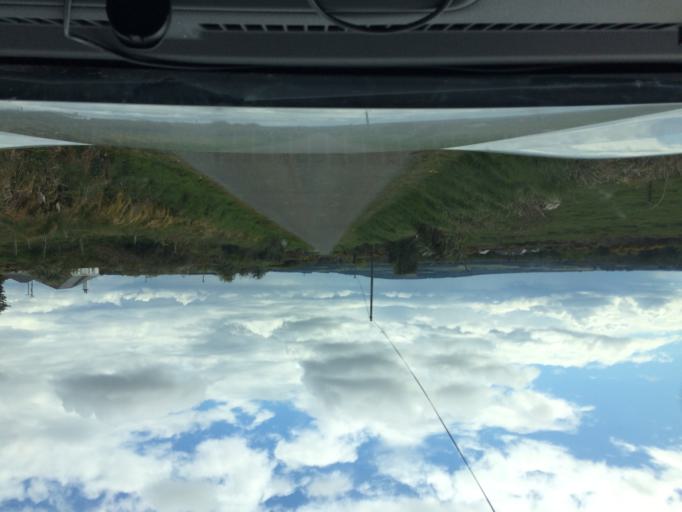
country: IE
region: Munster
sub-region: Waterford
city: Dungarvan
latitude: 52.0416
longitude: -7.6384
